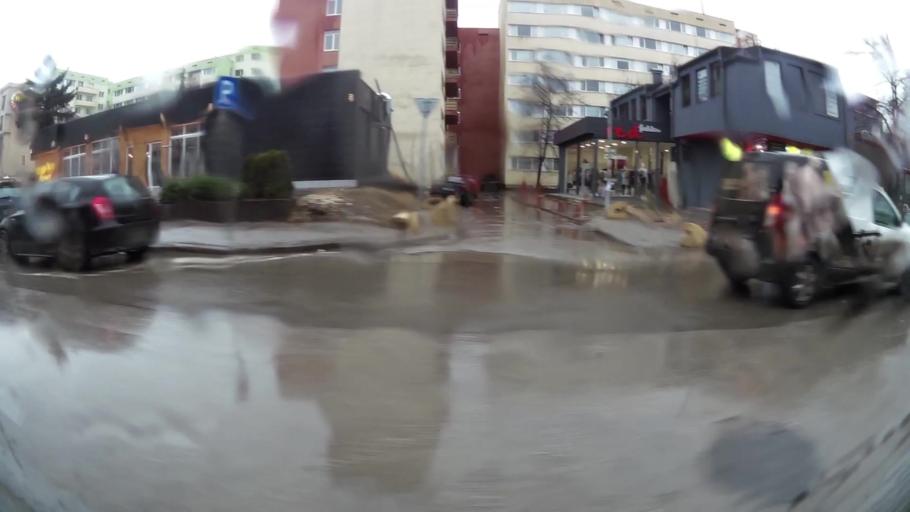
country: BG
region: Sofia-Capital
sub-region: Stolichna Obshtina
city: Sofia
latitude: 42.6528
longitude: 23.3425
